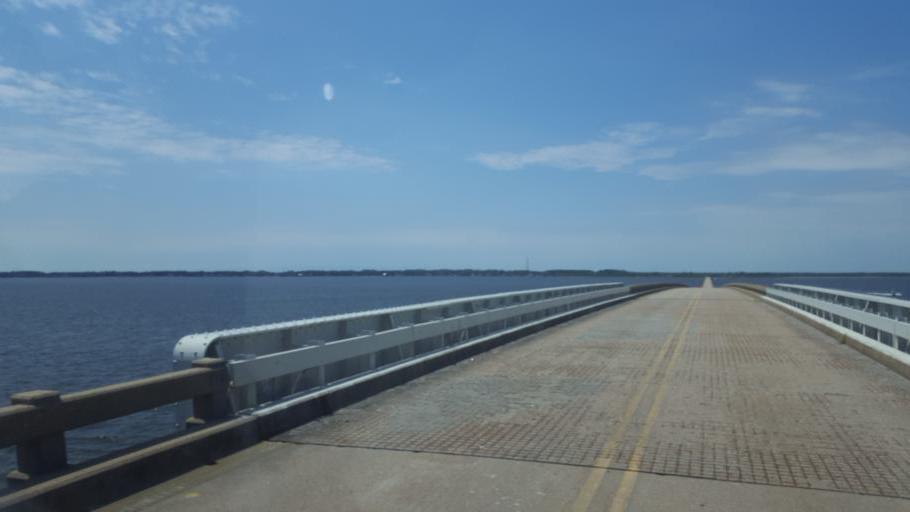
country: US
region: North Carolina
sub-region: Dare County
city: Manteo
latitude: 35.9190
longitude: -75.7480
